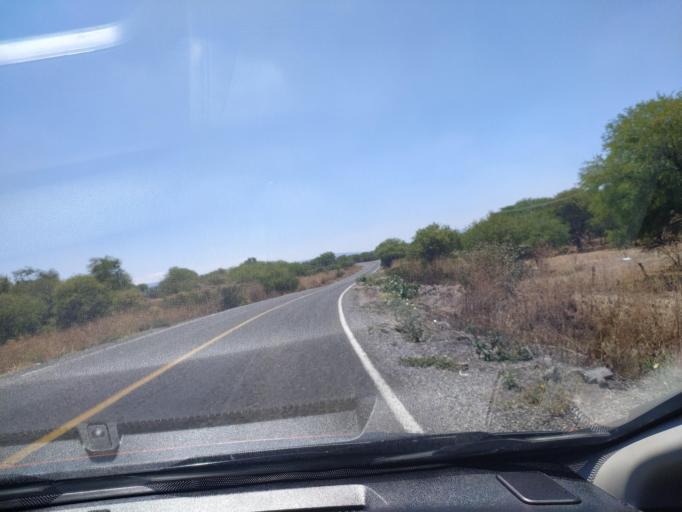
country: MX
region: Guanajuato
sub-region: San Francisco del Rincon
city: San Ignacio de Hidalgo
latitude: 20.7949
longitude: -101.8354
